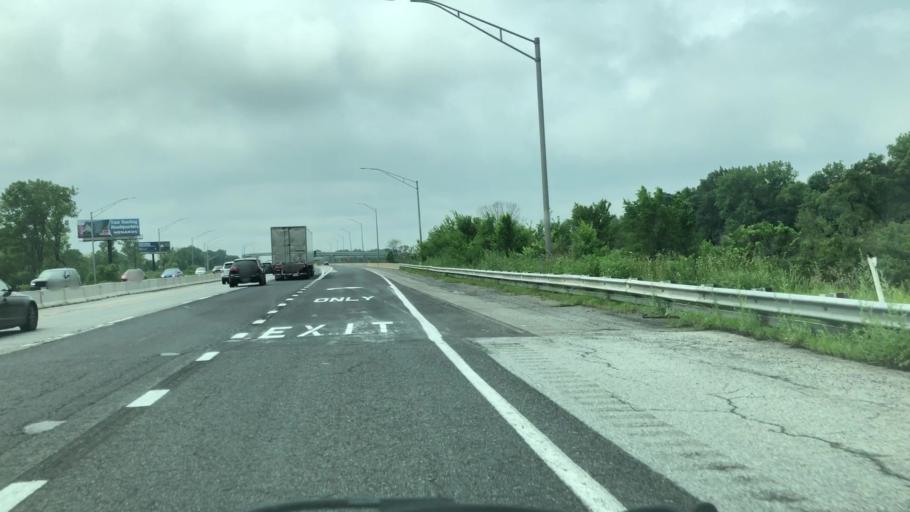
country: US
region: Indiana
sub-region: Lake County
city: East Chicago
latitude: 41.6088
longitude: -87.4124
